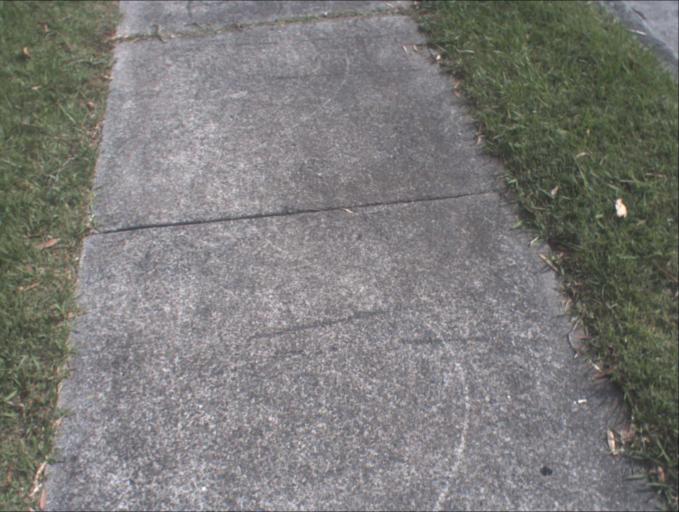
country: AU
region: Queensland
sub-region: Logan
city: Logan City
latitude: -27.6233
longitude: 153.1129
